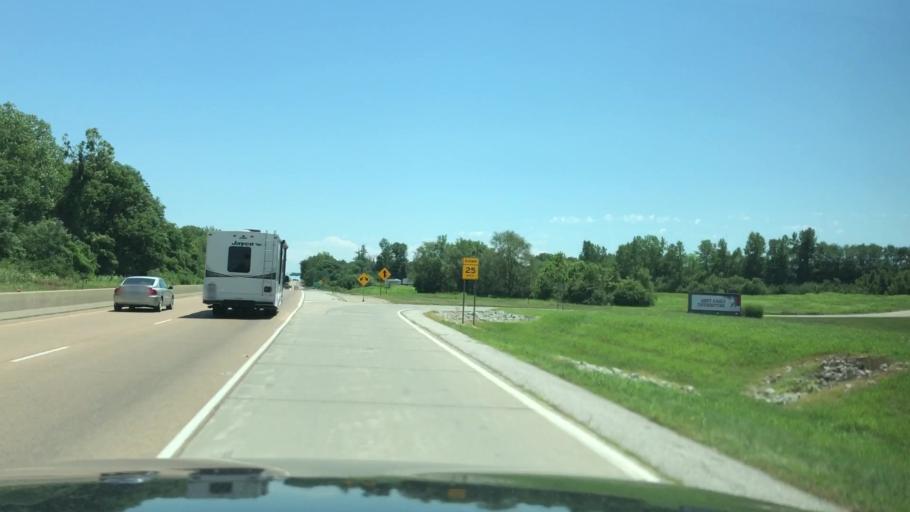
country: US
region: Illinois
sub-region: Saint Clair County
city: Alorton
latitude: 38.5562
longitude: -90.0790
